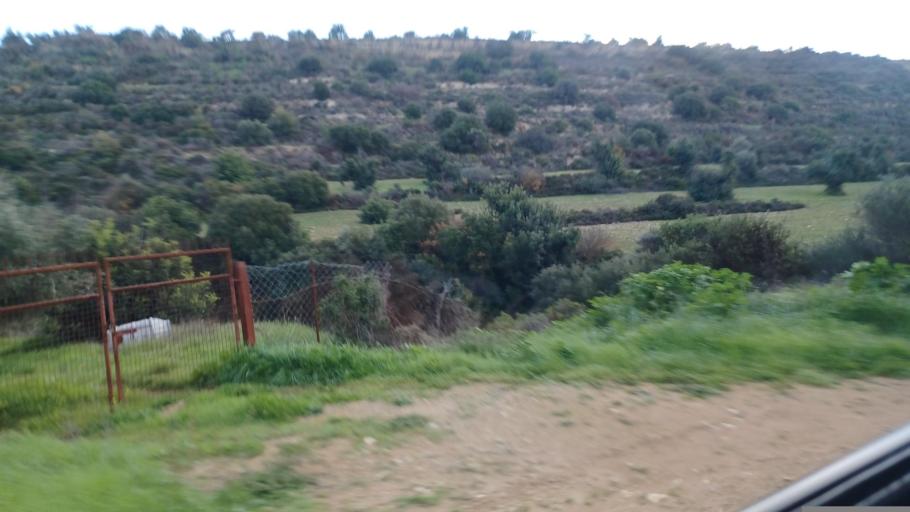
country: CY
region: Limassol
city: Pano Polemidia
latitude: 34.7631
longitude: 32.9789
